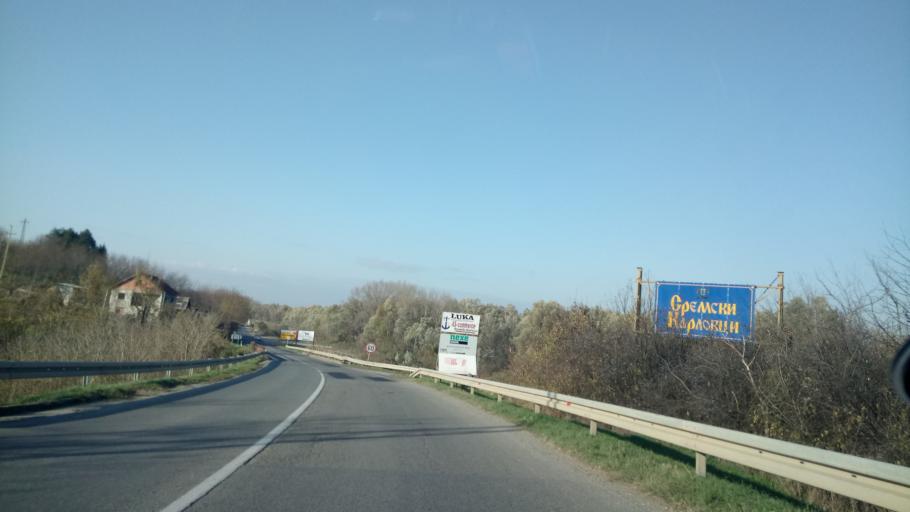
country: RS
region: Autonomna Pokrajina Vojvodina
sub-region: Juznobacki Okrug
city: Sremski Karlovci
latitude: 45.1909
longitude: 19.9531
